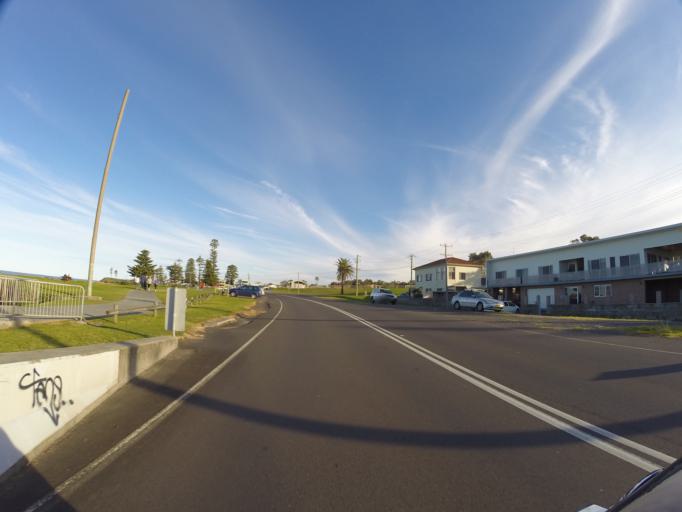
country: AU
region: New South Wales
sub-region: Wollongong
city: Bulli
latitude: -34.3343
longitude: 150.9240
